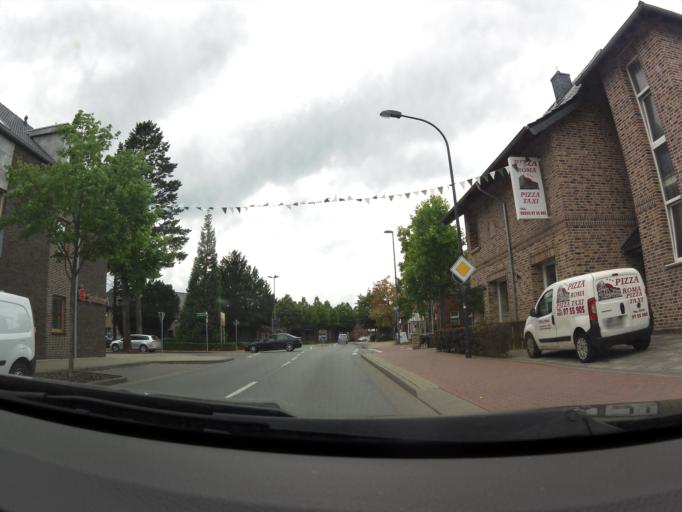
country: DE
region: North Rhine-Westphalia
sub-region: Regierungsbezirk Dusseldorf
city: Kevelaer
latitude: 51.5982
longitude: 6.2878
